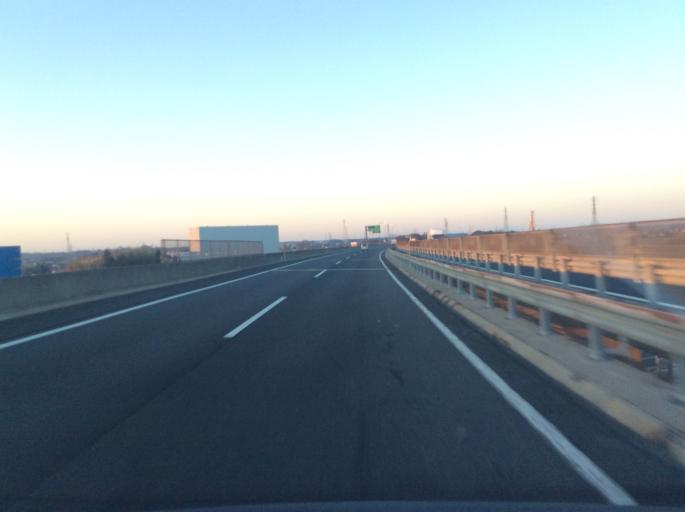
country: JP
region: Ibaraki
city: Funaishikawa
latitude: 36.5131
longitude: 140.5798
